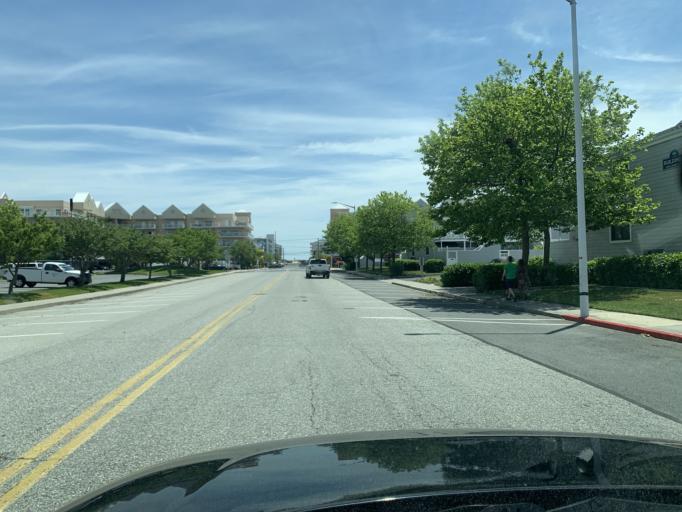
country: US
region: Maryland
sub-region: Worcester County
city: Ocean City
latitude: 38.4307
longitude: -75.0584
